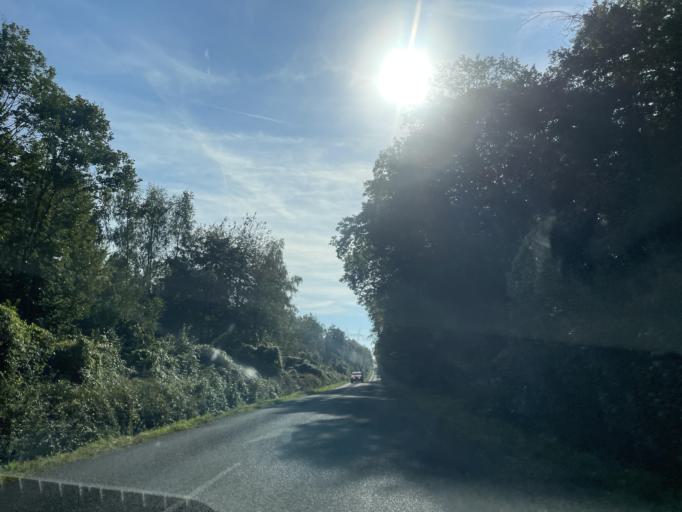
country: FR
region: Ile-de-France
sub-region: Departement de Seine-et-Marne
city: Saint-Jean-les-Deux-Jumeaux
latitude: 48.9525
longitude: 2.9884
